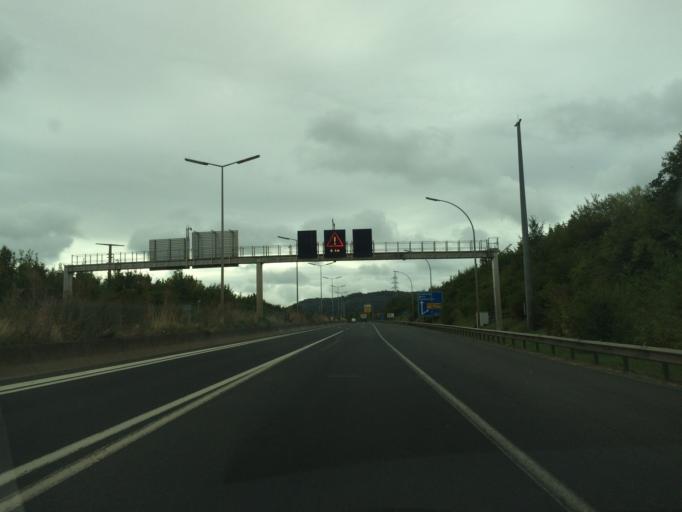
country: LU
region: Luxembourg
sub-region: Canton d'Esch-sur-Alzette
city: Schifflange
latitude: 49.5177
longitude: 6.0075
